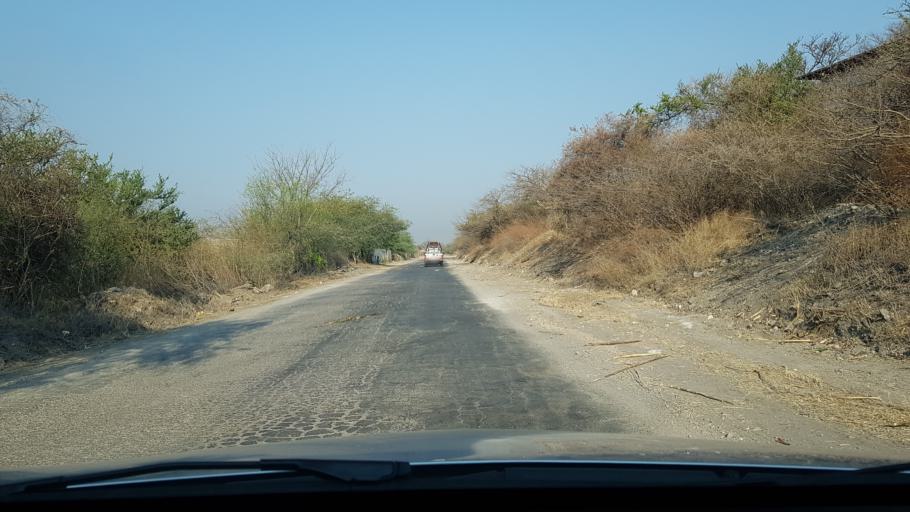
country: MX
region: Morelos
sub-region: Tlaltizapan de Zapata
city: Colonia Palo Prieto (Chipitongo)
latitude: 18.6918
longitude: -99.0978
